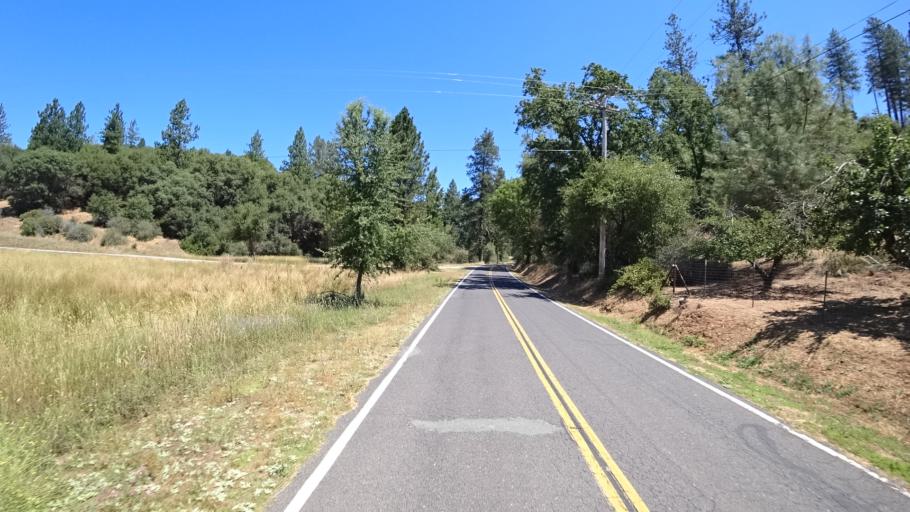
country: US
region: California
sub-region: Calaveras County
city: Mountain Ranch
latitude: 38.2087
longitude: -120.5513
